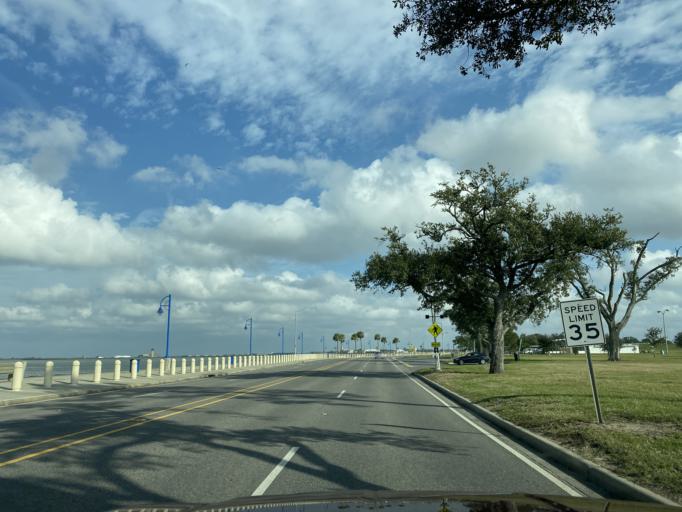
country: US
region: Louisiana
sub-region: Orleans Parish
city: New Orleans
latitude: 30.0353
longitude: -90.0454
